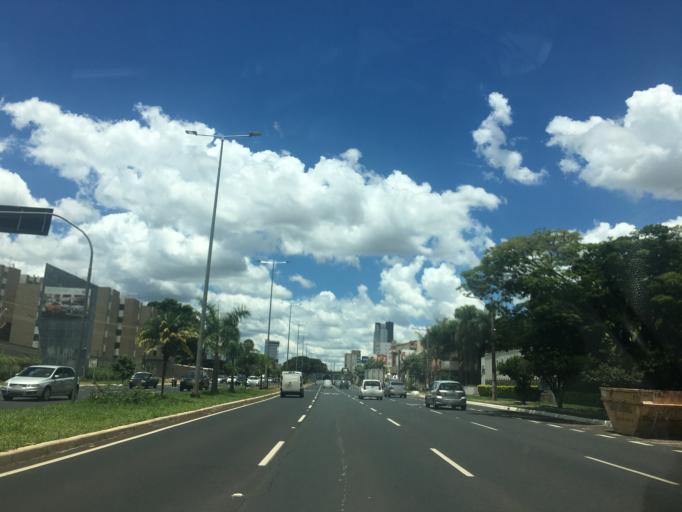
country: BR
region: Minas Gerais
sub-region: Uberlandia
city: Uberlandia
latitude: -18.9217
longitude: -48.2693
